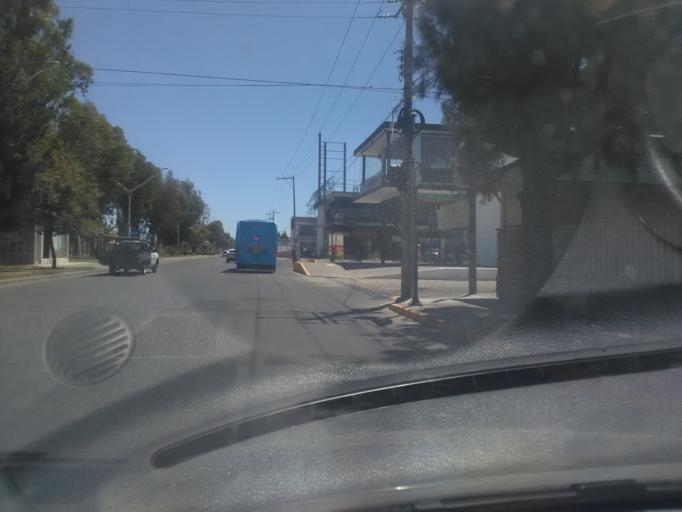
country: MX
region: Durango
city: Victoria de Durango
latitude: 24.0066
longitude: -104.6626
